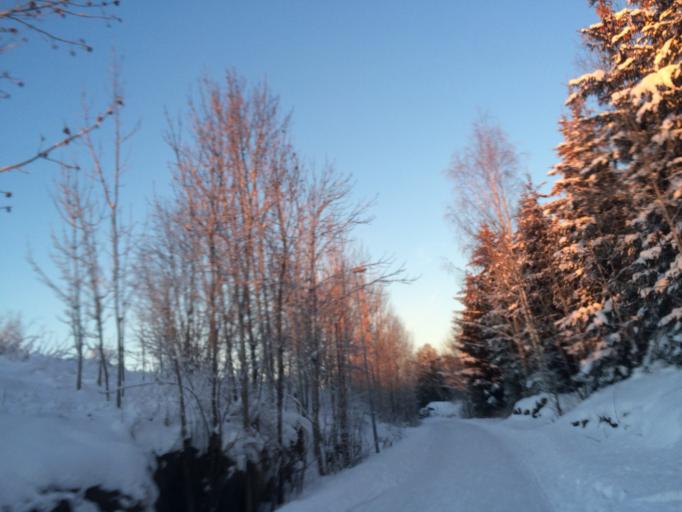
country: NO
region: Akershus
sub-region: Ski
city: Ski
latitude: 59.7055
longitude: 10.8344
